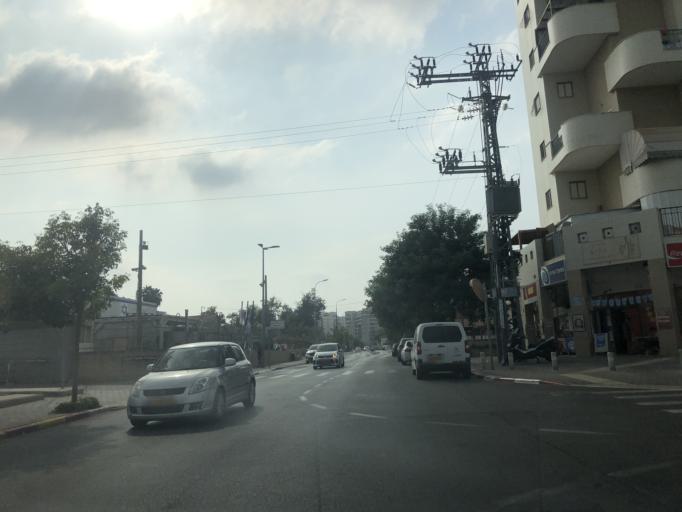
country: IL
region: Central District
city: Rosh Ha'Ayin
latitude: 32.0991
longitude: 34.9456
